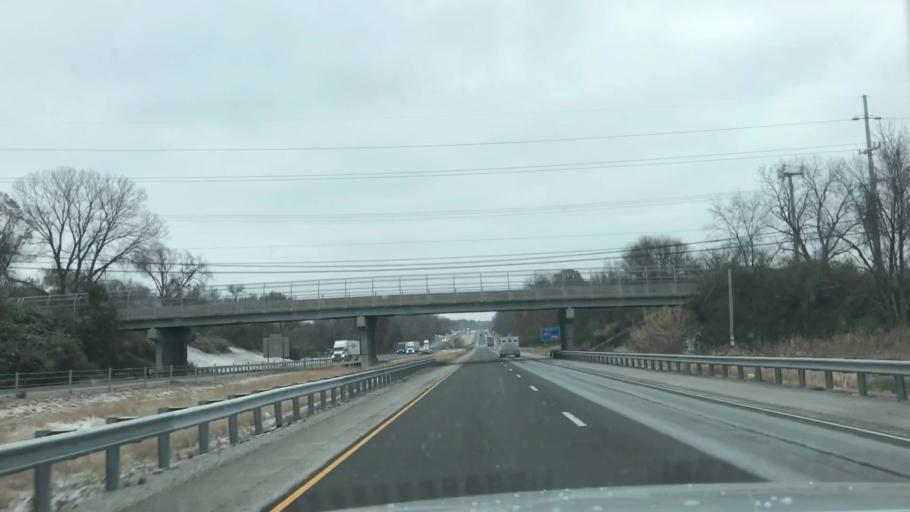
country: US
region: Illinois
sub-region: Madison County
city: Glen Carbon
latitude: 38.7566
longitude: -89.9853
